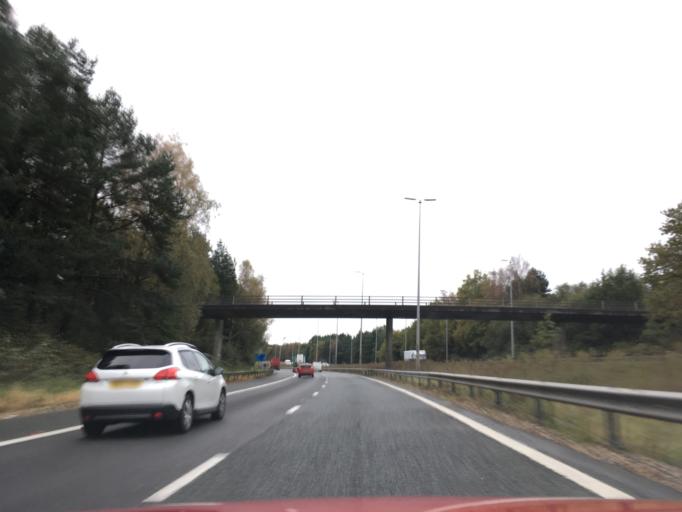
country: GB
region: England
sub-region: Hampshire
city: Eastleigh
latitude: 50.9576
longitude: -1.3979
